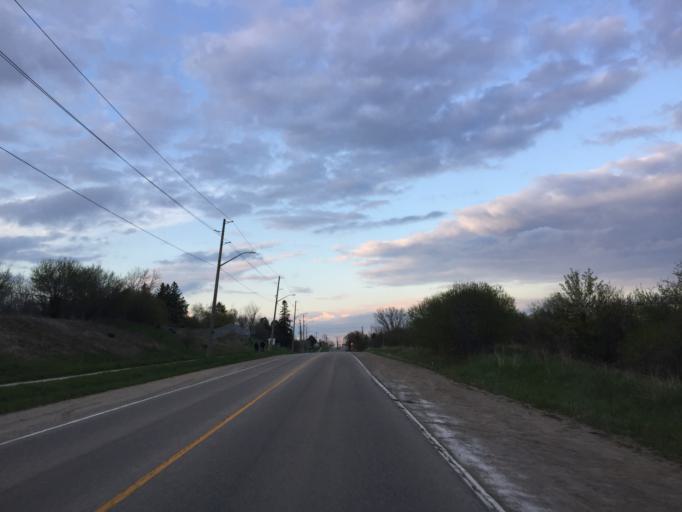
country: CA
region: Ontario
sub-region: Wellington County
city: Guelph
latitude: 43.5114
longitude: -80.2452
